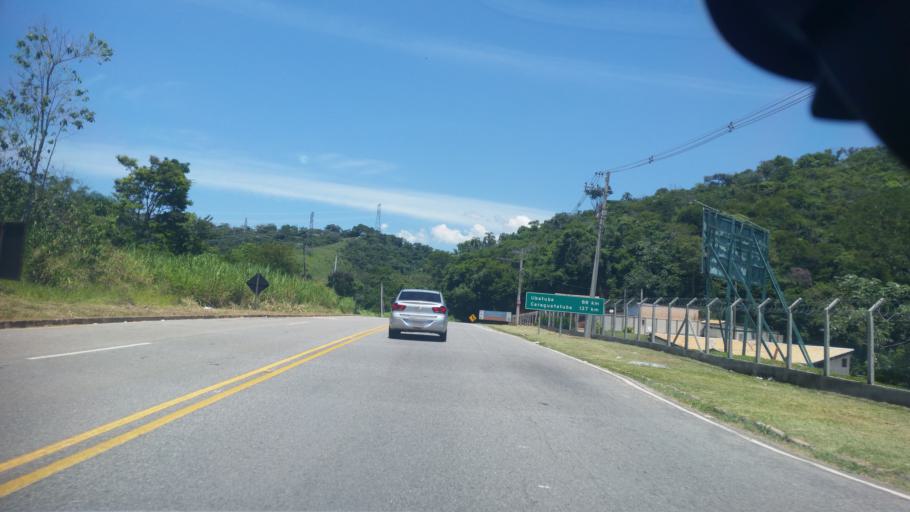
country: BR
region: Sao Paulo
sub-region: Taubate
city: Taubate
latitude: -23.0914
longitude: -45.5414
